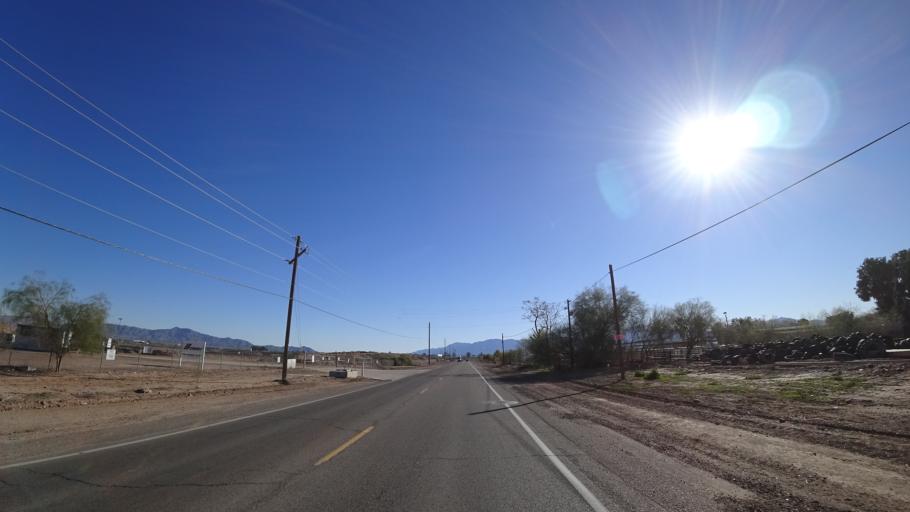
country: US
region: Arizona
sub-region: Maricopa County
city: Laveen
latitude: 33.4046
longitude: -112.2041
